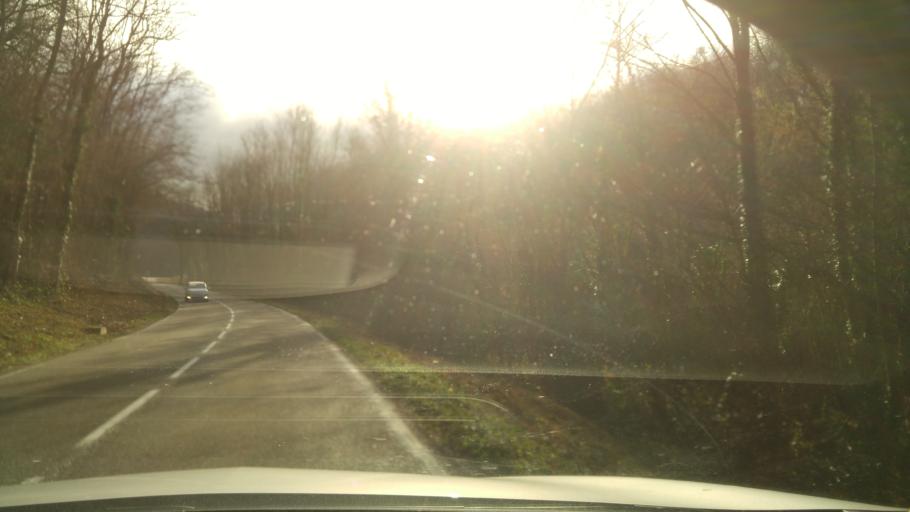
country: FR
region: Rhone-Alpes
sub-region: Departement de l'Isere
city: Roche
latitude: 45.5995
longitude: 5.1633
